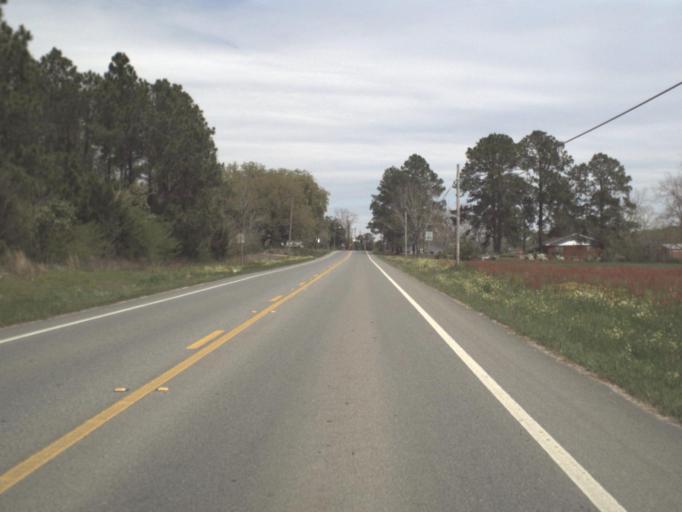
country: US
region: Florida
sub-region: Jackson County
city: Graceville
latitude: 30.9460
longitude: -85.4059
